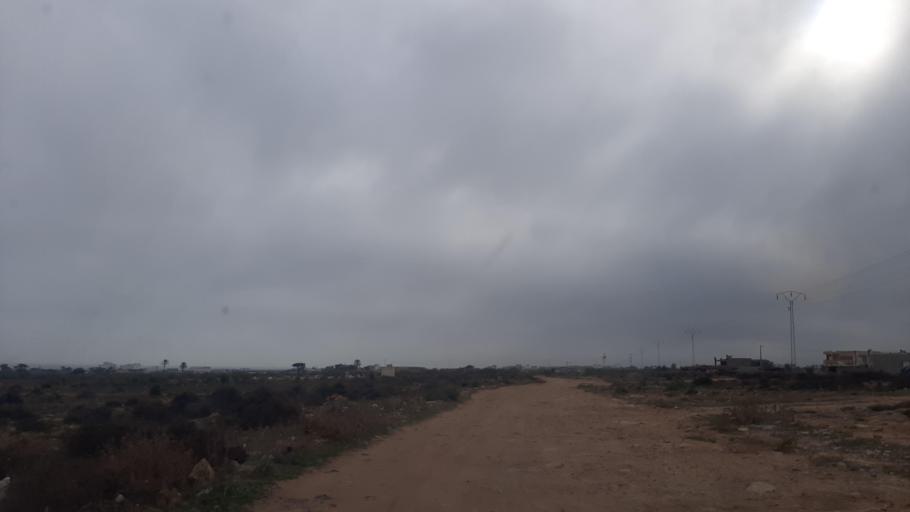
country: TN
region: Nabul
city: Menzel Heurr
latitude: 36.6929
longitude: 10.9356
